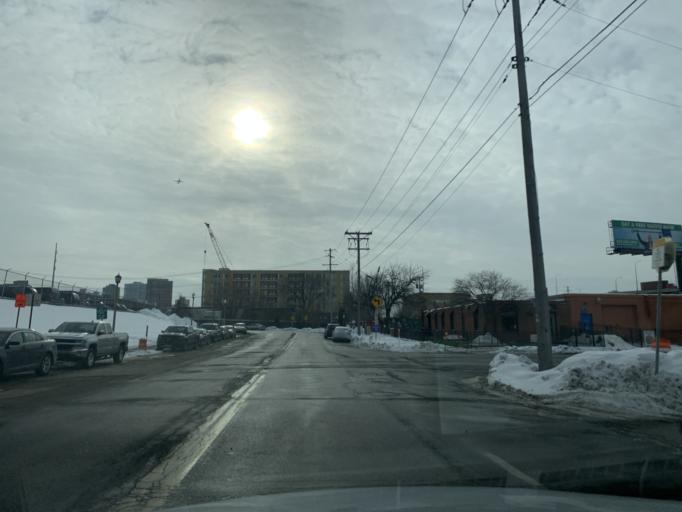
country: US
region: Minnesota
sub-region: Hennepin County
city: Minneapolis
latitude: 44.9810
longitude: -93.2853
